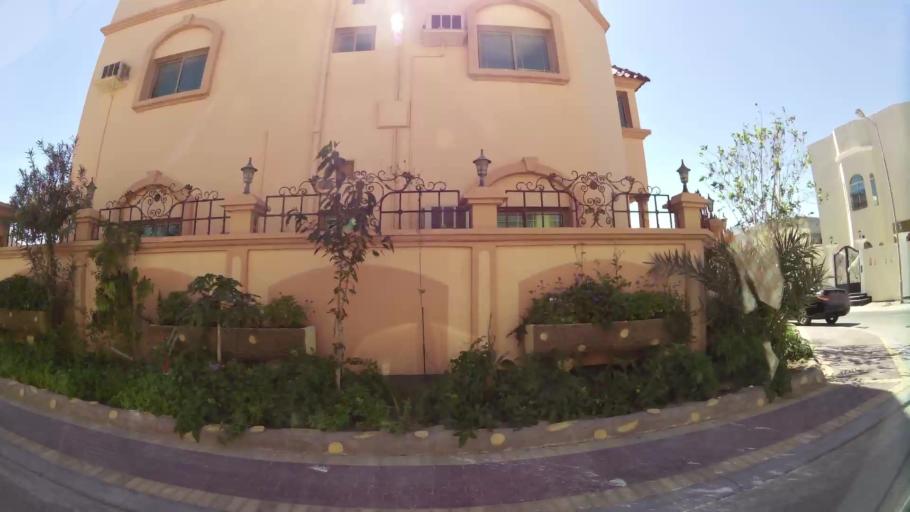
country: BH
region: Muharraq
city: Al Hadd
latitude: 26.2800
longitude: 50.6424
